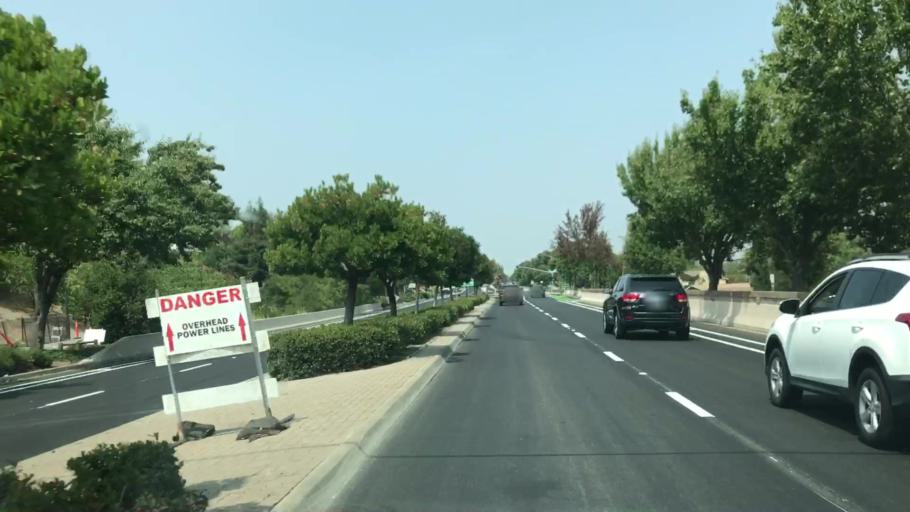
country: US
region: California
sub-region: Alameda County
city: Dublin
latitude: 37.7155
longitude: -121.9400
